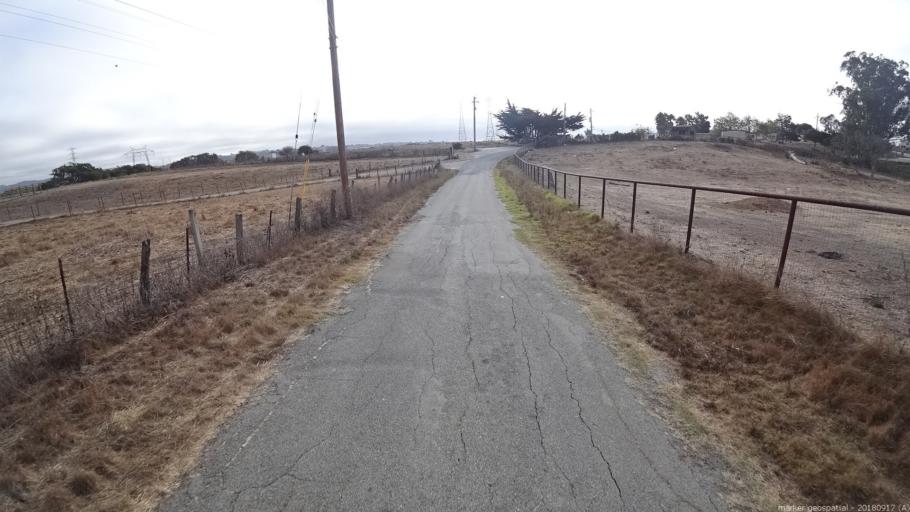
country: US
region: California
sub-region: Monterey County
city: Elkhorn
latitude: 36.7990
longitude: -121.7424
